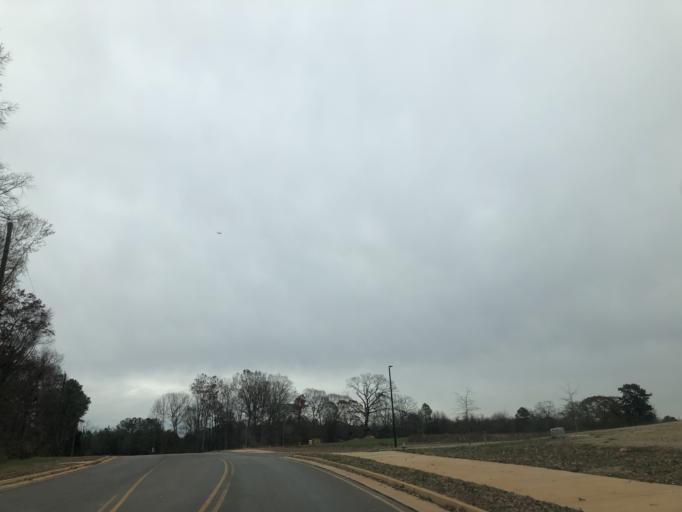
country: US
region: Georgia
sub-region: Clayton County
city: Conley
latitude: 33.6178
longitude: -84.2704
